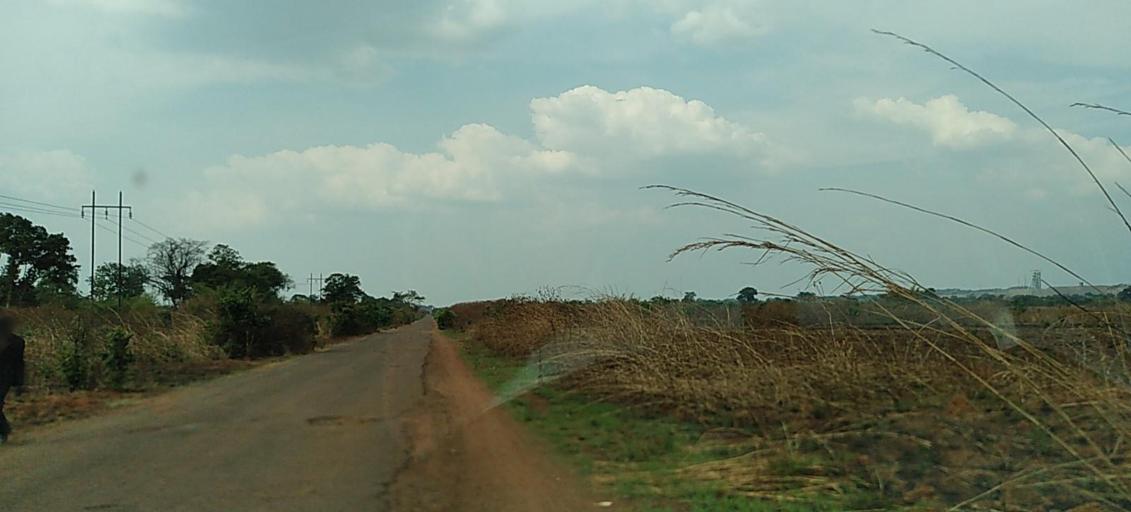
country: ZM
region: Copperbelt
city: Chililabombwe
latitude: -12.3910
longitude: 27.8071
